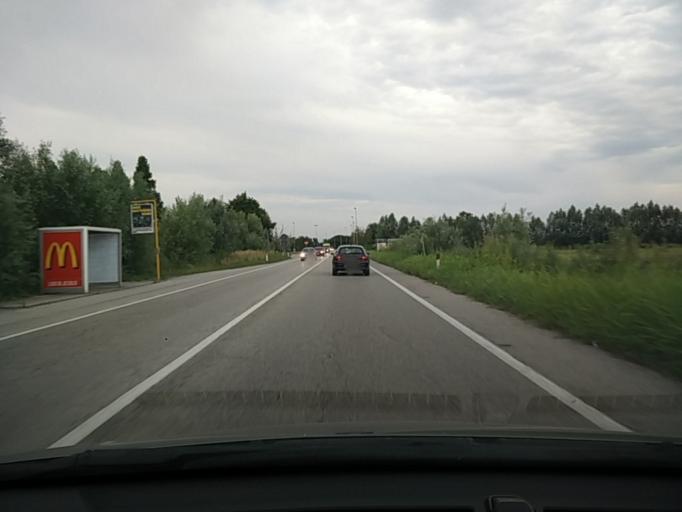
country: IT
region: Veneto
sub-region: Provincia di Venezia
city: Passarella
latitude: 45.5595
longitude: 12.5754
